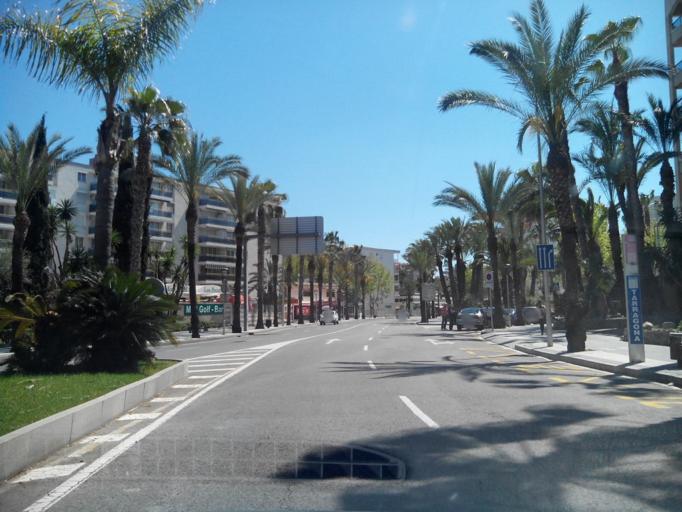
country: ES
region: Catalonia
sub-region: Provincia de Tarragona
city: Salou
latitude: 41.0759
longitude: 1.1443
